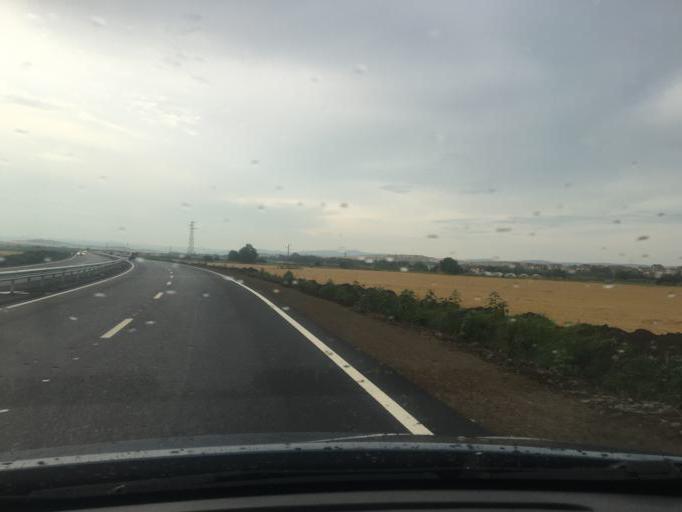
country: BG
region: Burgas
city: Aheloy
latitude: 42.6400
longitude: 27.6390
